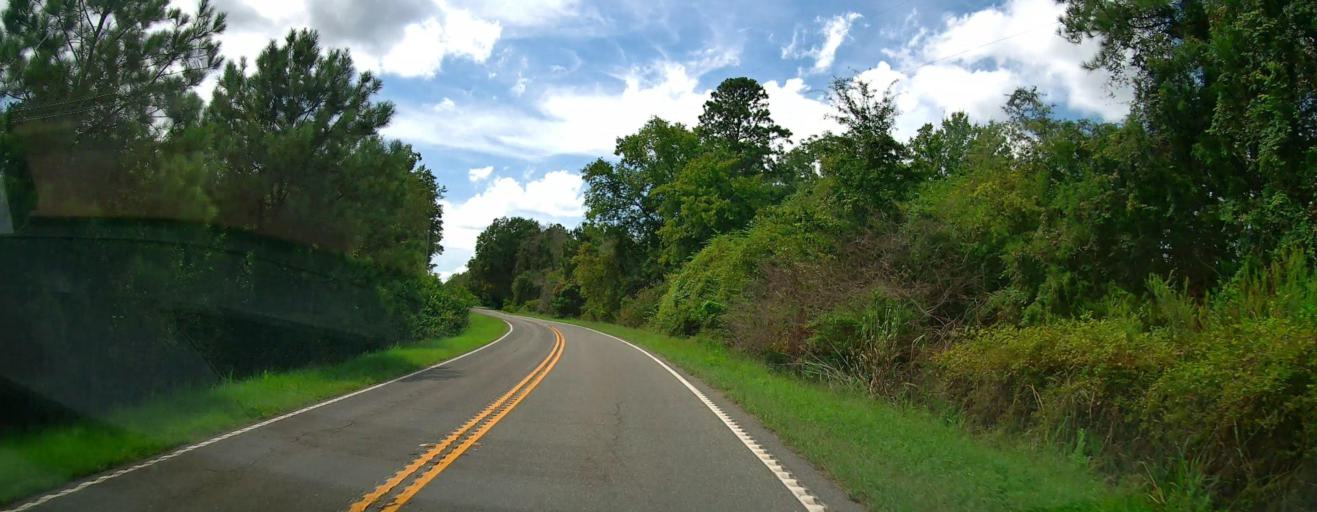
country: US
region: Georgia
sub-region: Taylor County
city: Reynolds
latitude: 32.4411
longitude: -84.1085
